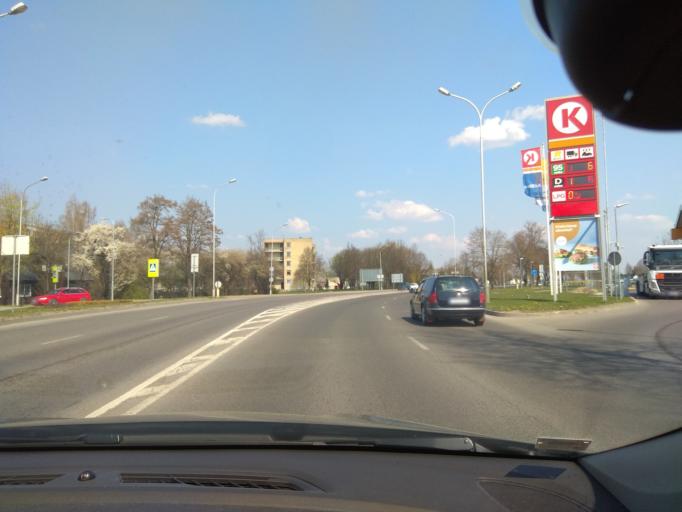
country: LT
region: Marijampoles apskritis
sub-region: Marijampole Municipality
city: Marijampole
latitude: 54.5760
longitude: 23.3708
